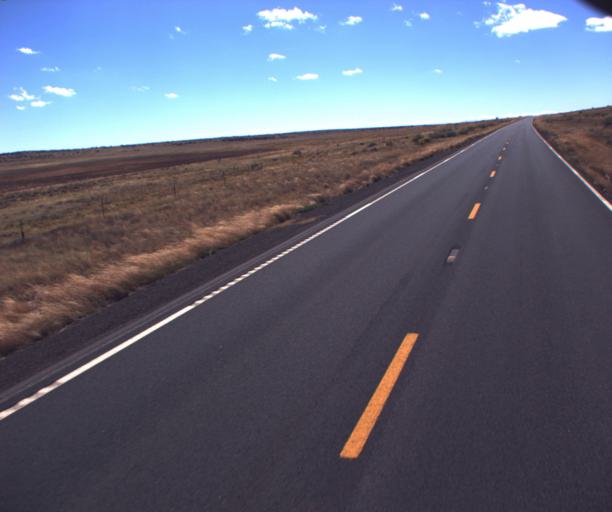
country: US
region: Arizona
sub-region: Apache County
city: Houck
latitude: 34.9803
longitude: -109.2270
